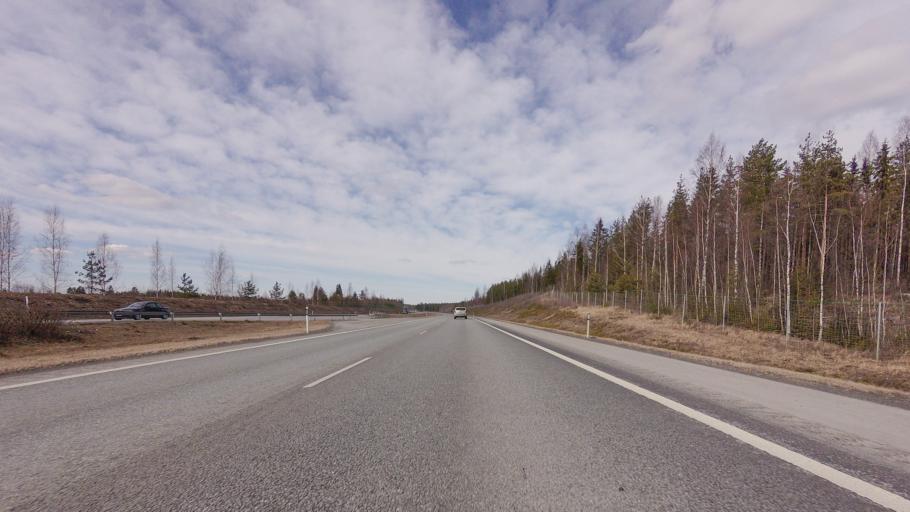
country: FI
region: Pirkanmaa
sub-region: Etelae-Pirkanmaa
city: Viiala
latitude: 61.2621
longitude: 23.8314
